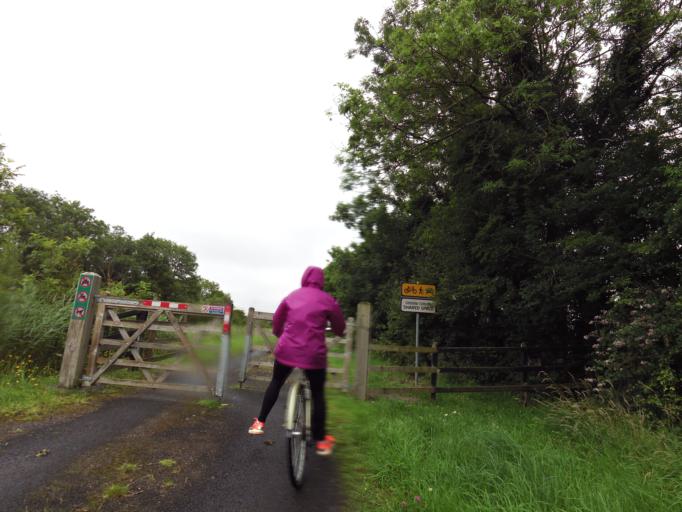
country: IE
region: Leinster
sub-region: An Longfort
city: Edgeworthstown
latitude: 53.5804
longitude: -7.5659
